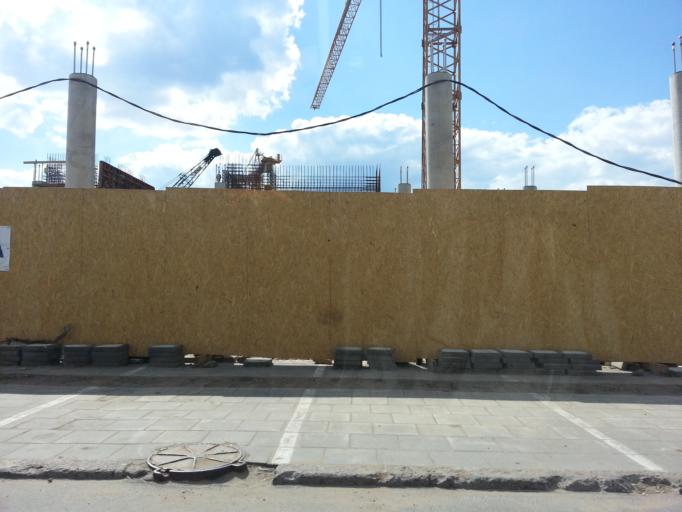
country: LT
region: Vilnius County
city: Vilkpede
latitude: 54.6697
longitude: 25.2604
